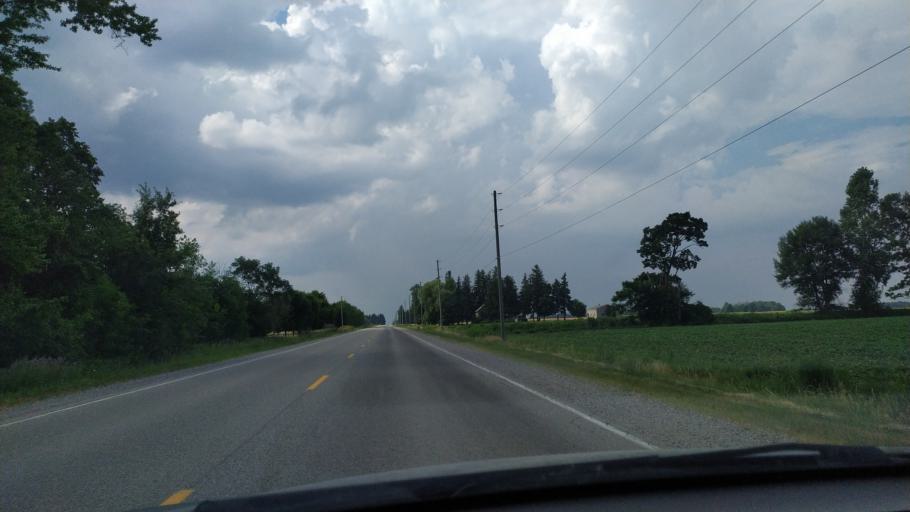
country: CA
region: Ontario
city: London
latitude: 43.1153
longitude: -81.1637
